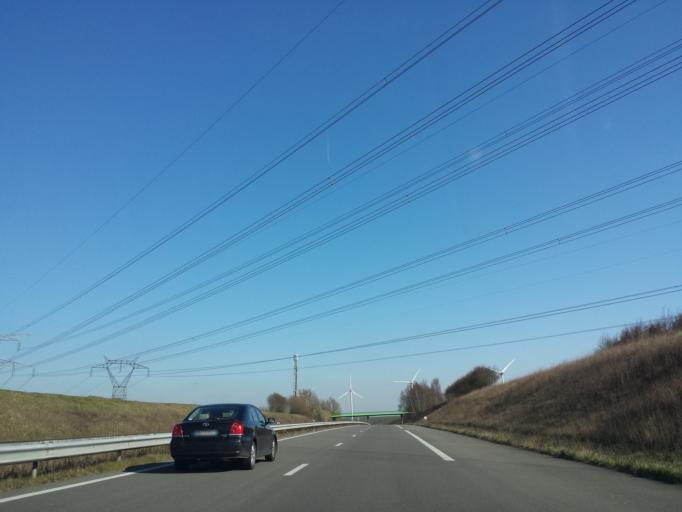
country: FR
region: Picardie
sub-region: Departement de la Somme
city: Conty
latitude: 49.6843
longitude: 2.2208
